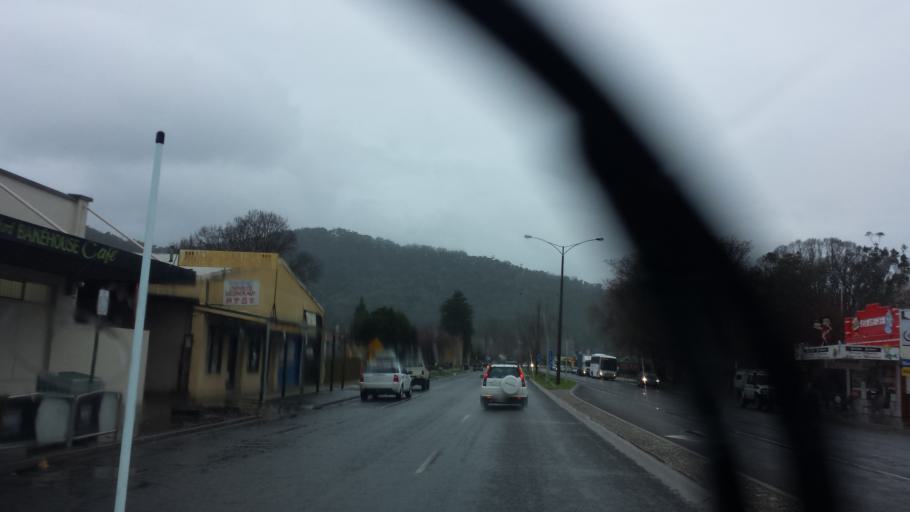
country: AU
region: Victoria
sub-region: Wangaratta
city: Wangaratta
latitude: -36.5608
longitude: 146.7240
